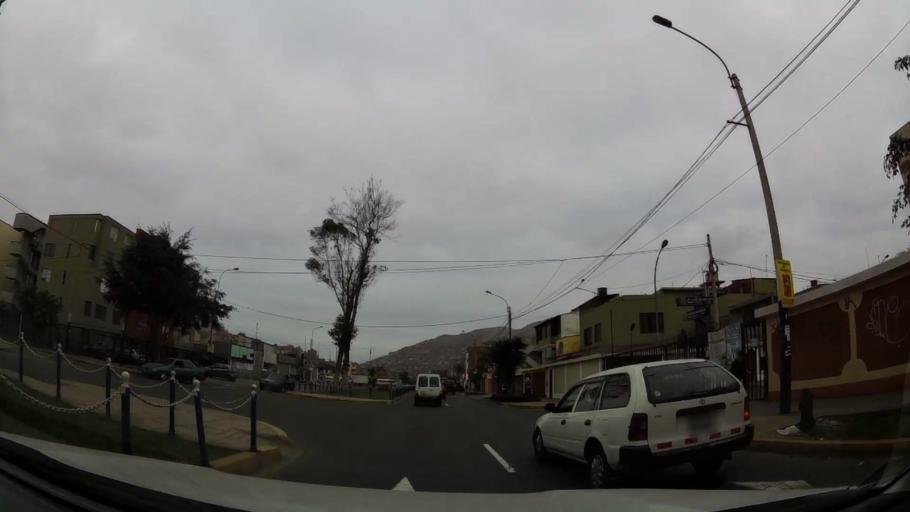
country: PE
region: Lima
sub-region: Lima
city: Surco
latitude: -12.1804
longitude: -77.0115
